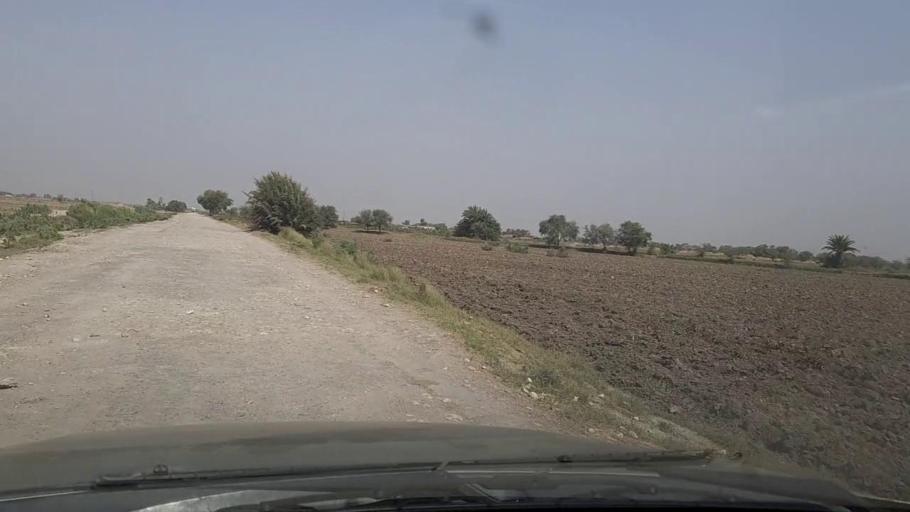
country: PK
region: Sindh
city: Thul
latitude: 28.4079
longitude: 68.6999
